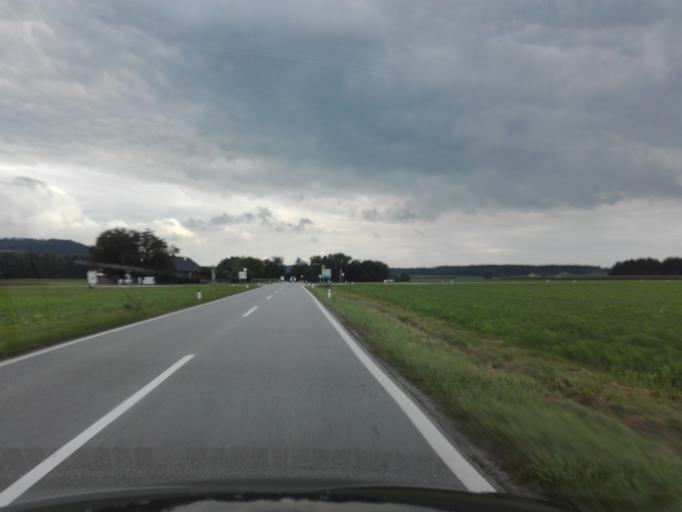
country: DE
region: Bavaria
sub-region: Lower Bavaria
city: Bad Fussing
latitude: 48.2687
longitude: 13.3297
